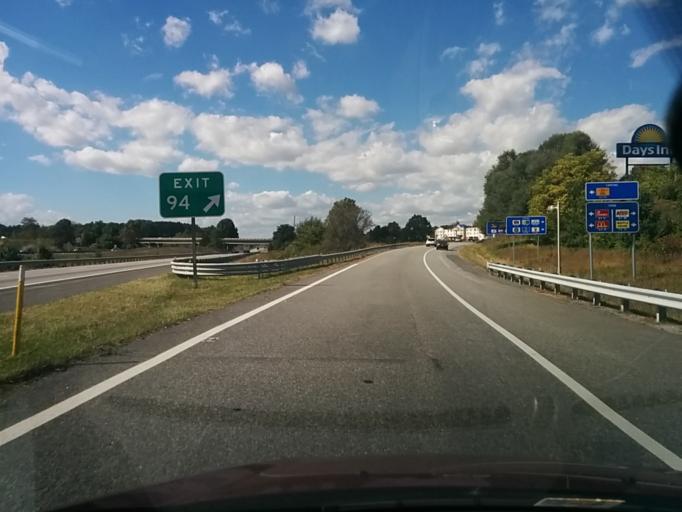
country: US
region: Virginia
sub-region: Augusta County
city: Lyndhurst
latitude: 38.0600
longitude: -78.9369
